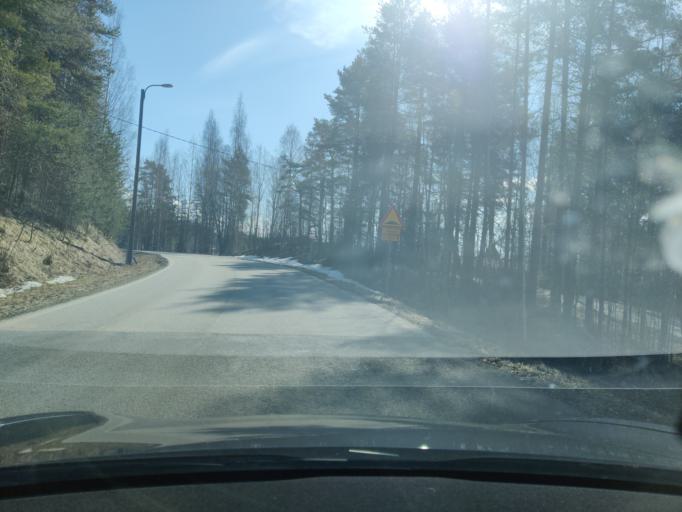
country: FI
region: Northern Savo
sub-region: Kuopio
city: Vehmersalmi
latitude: 62.7668
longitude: 28.0131
